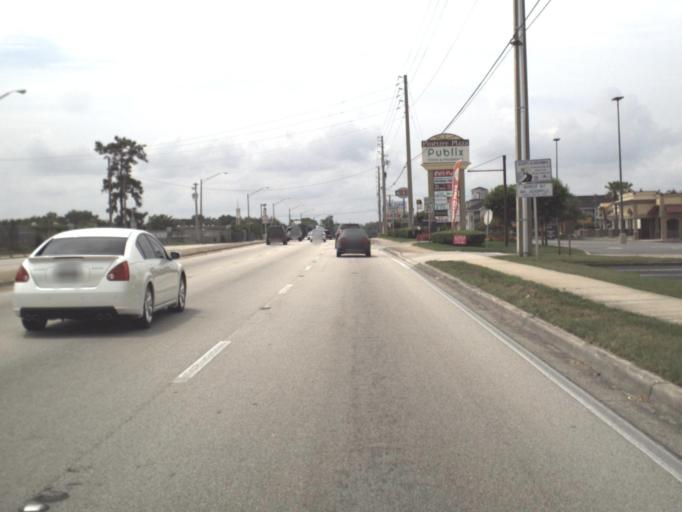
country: US
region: Florida
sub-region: Clay County
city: Bellair-Meadowbrook Terrace
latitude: 30.1641
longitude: -81.7477
